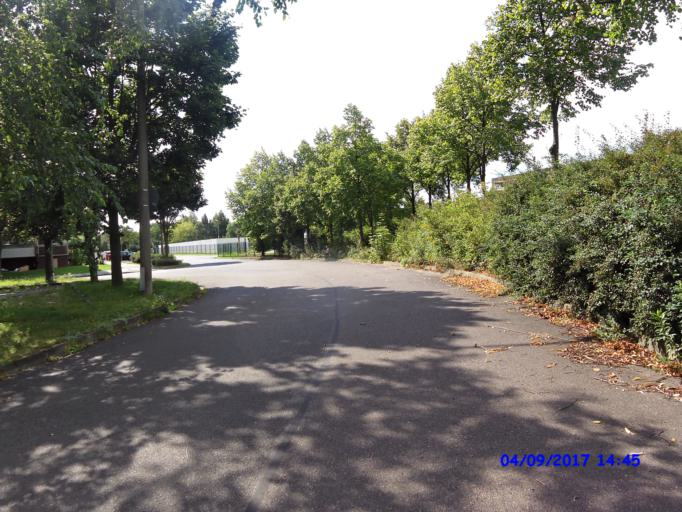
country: DE
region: Saxony
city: Taucha
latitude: 51.3578
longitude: 12.4622
